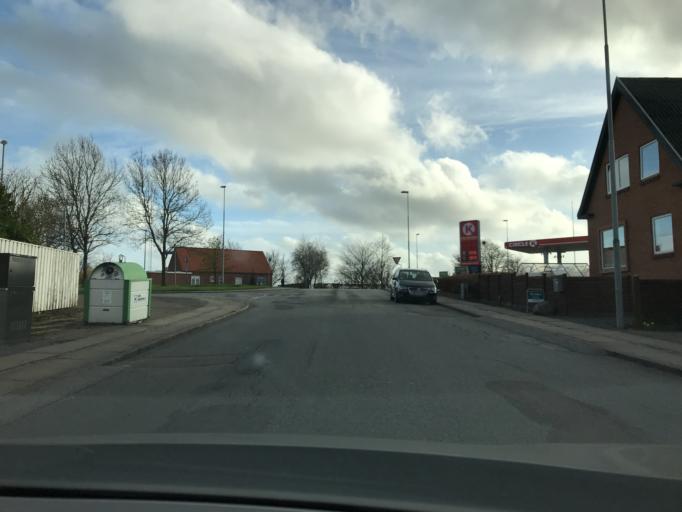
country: DK
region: Central Jutland
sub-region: Skive Kommune
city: Skive
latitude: 56.5698
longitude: 9.0119
